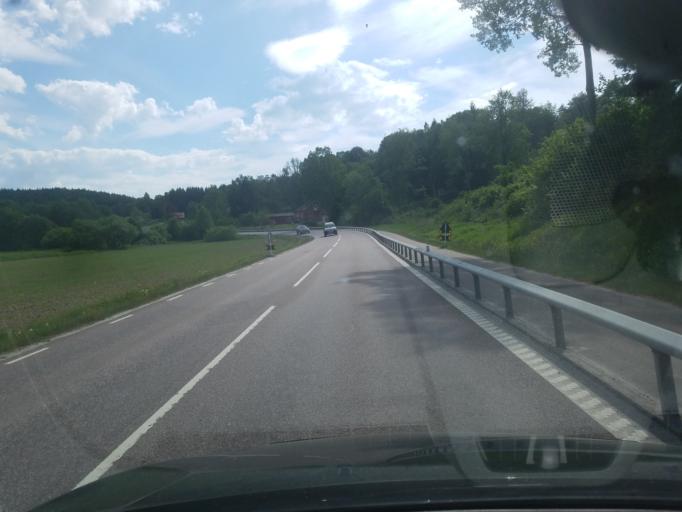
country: SE
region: Vaestra Goetaland
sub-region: Kungalvs Kommun
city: Diserod
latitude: 57.9068
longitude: 12.0089
